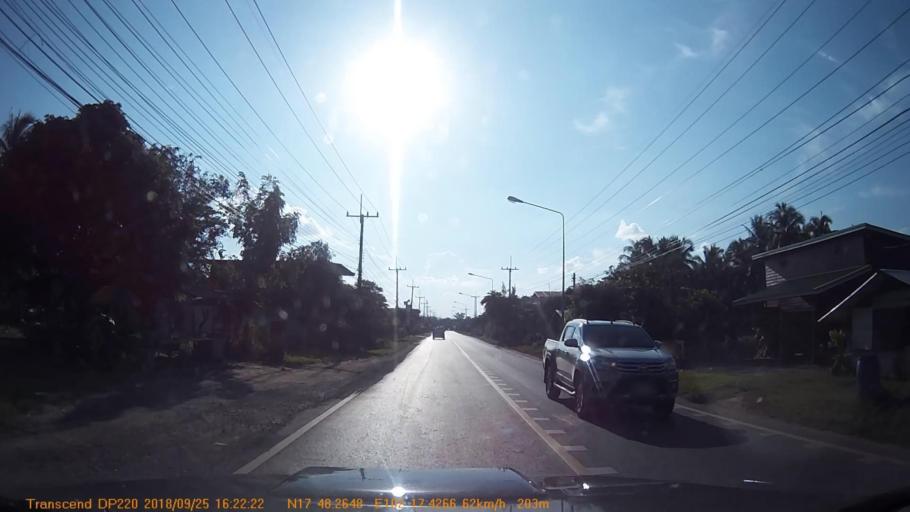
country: TH
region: Changwat Udon Thani
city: Nam Som
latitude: 17.8044
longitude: 102.2905
